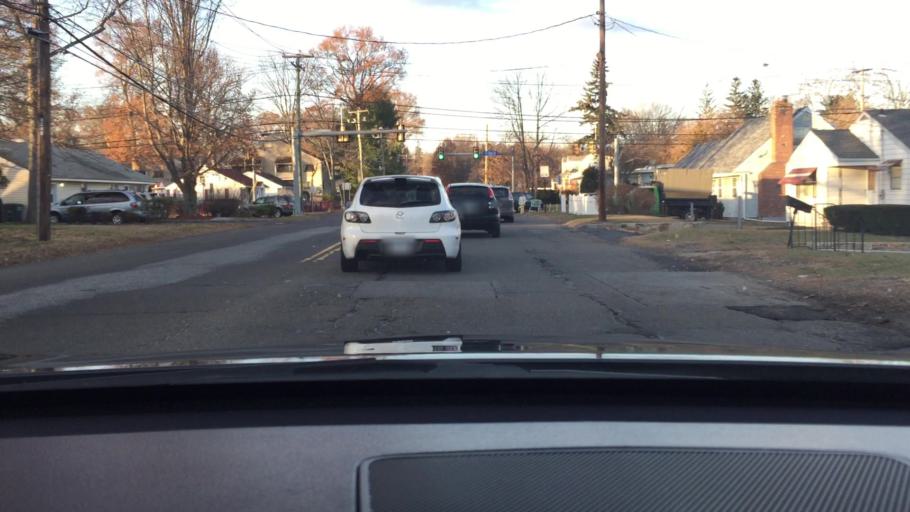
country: US
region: Connecticut
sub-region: Fairfield County
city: Trumbull
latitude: 41.2253
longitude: -73.2318
